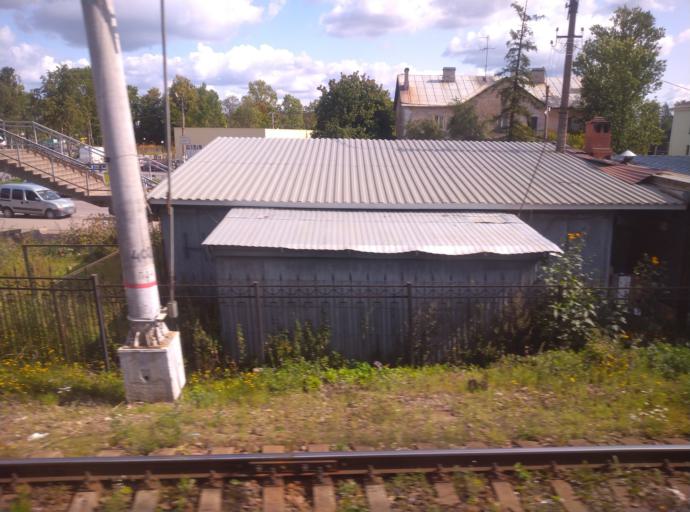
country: RU
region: Leningrad
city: Ul'yanovka
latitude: 59.6358
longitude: 30.7572
